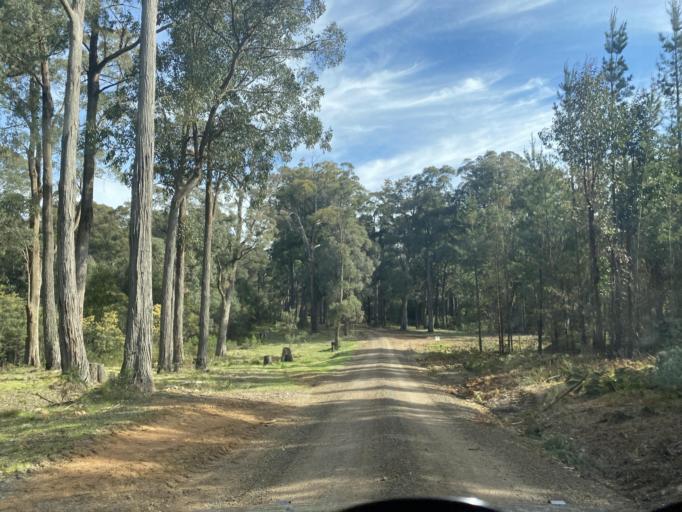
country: AU
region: Victoria
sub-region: Mansfield
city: Mansfield
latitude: -36.8427
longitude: 146.1825
